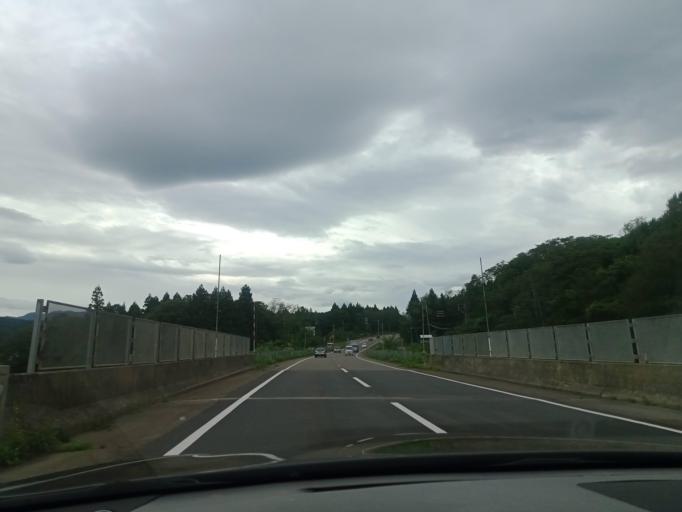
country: JP
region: Niigata
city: Arai
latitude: 36.9669
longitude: 138.2249
